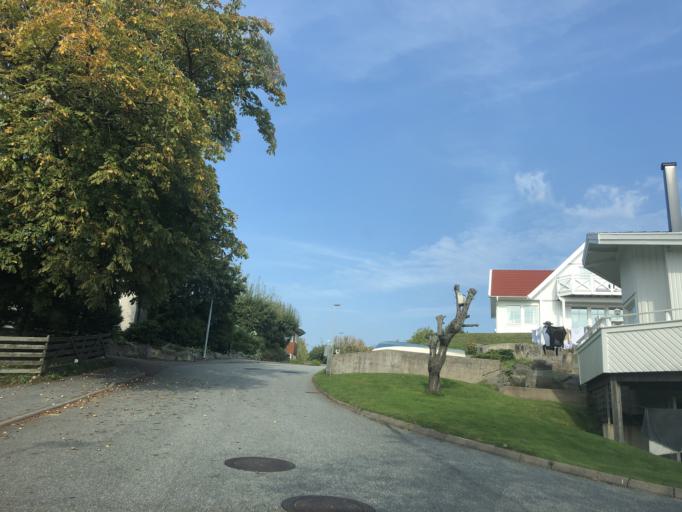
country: SE
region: Vaestra Goetaland
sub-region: Goteborg
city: Majorna
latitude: 57.6437
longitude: 11.8776
